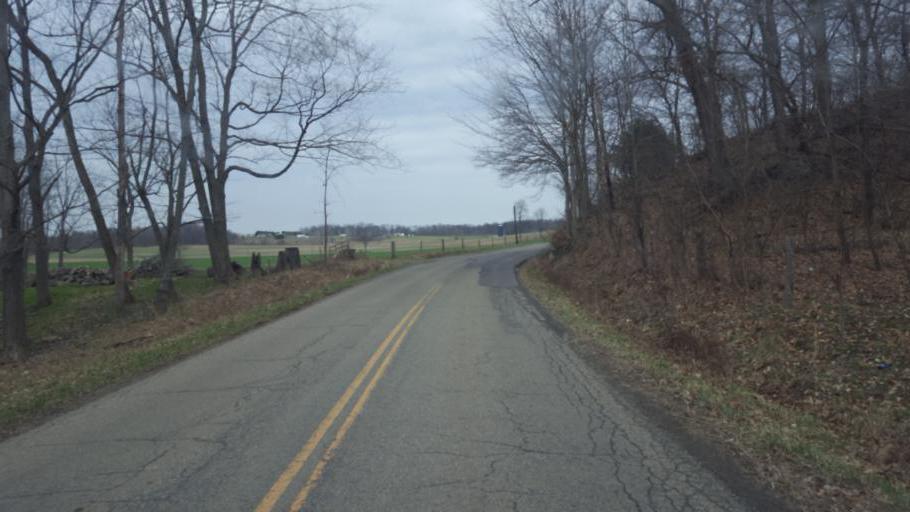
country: US
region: Ohio
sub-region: Knox County
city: Fredericktown
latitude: 40.5131
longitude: -82.4141
